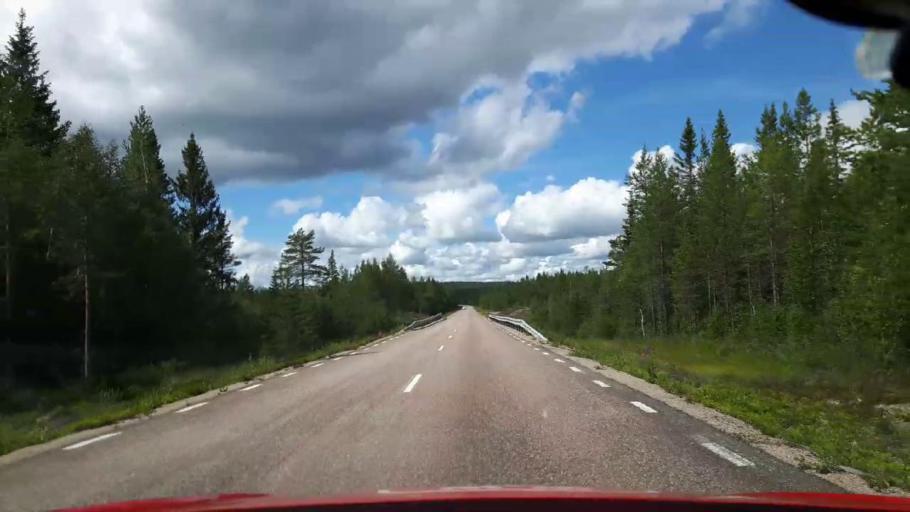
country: SE
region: Jaemtland
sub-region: Harjedalens Kommun
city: Sveg
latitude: 61.8332
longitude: 13.9121
